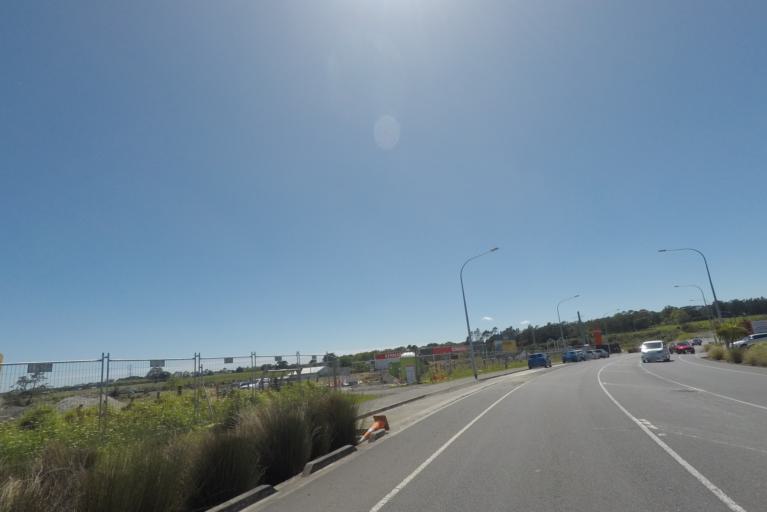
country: NZ
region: Auckland
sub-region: Auckland
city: Rosebank
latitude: -36.8082
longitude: 174.6039
